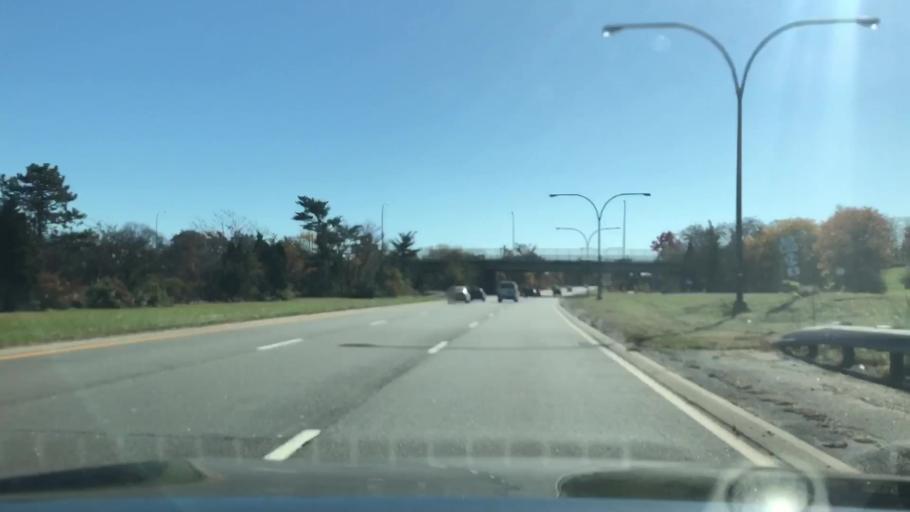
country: US
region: New York
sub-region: Nassau County
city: East Garden City
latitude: 40.7309
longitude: -73.5824
